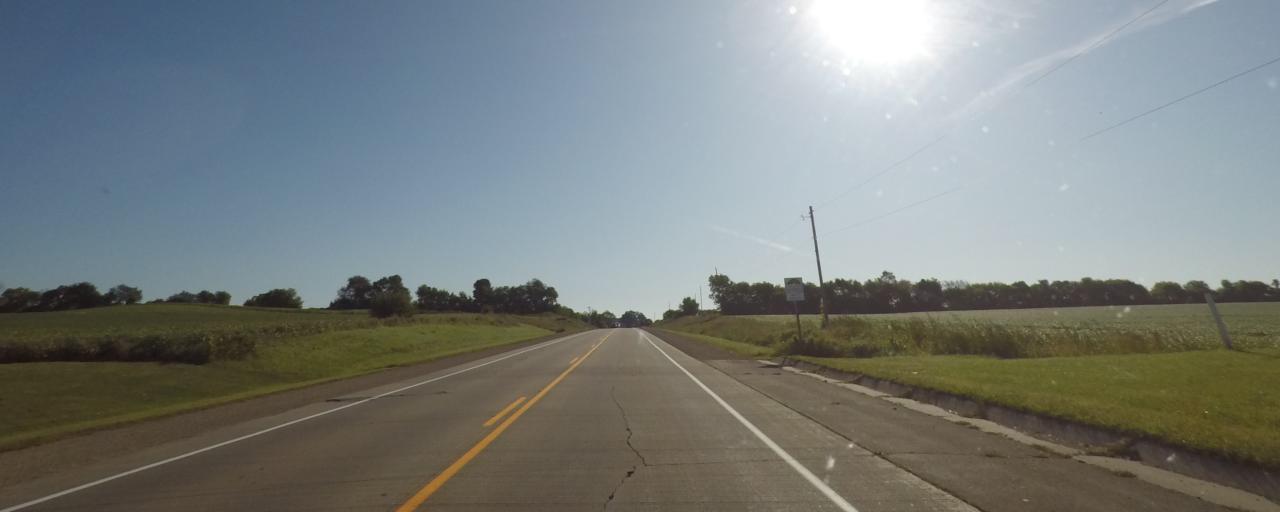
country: US
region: Wisconsin
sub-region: Dane County
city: Deerfield
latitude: 43.0365
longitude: -89.1062
